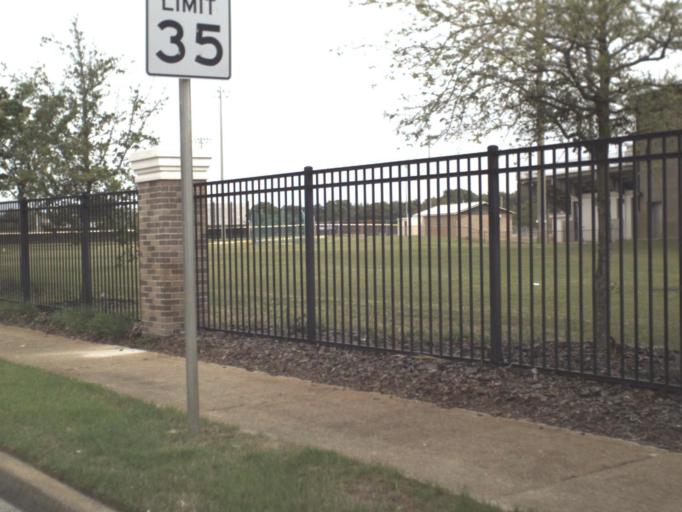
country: US
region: Florida
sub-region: Santa Rosa County
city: Gulf Breeze
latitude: 30.3615
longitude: -87.1682
